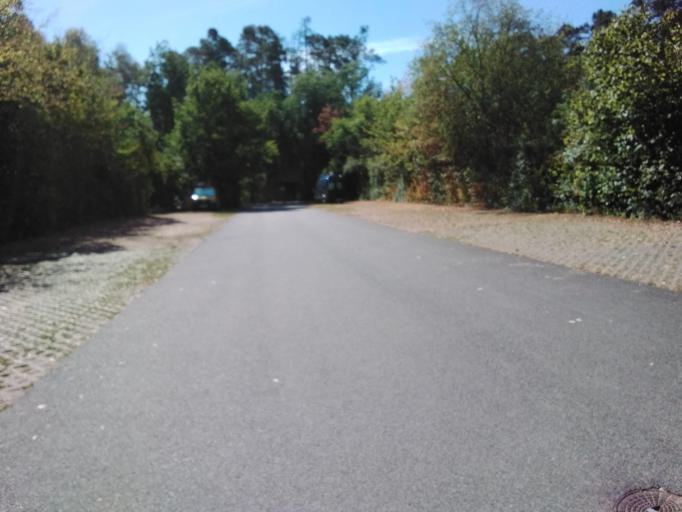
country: DE
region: Bavaria
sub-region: Regierungsbezirk Mittelfranken
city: Hilpoltstein
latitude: 49.2267
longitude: 11.1967
